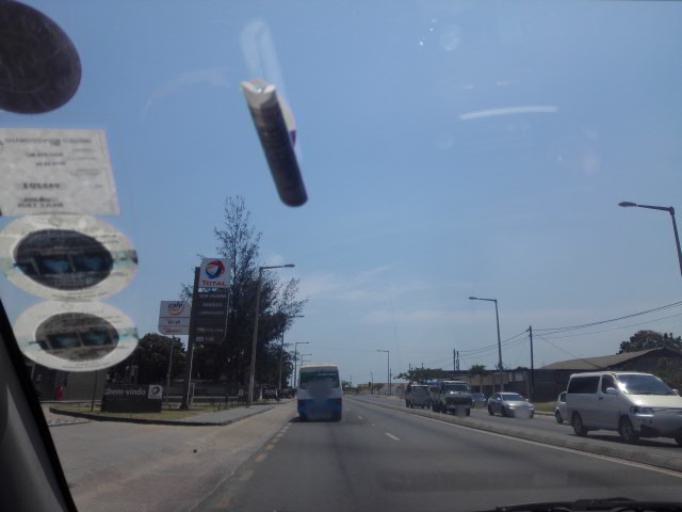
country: MZ
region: Maputo City
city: Maputo
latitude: -25.9202
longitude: 32.5638
